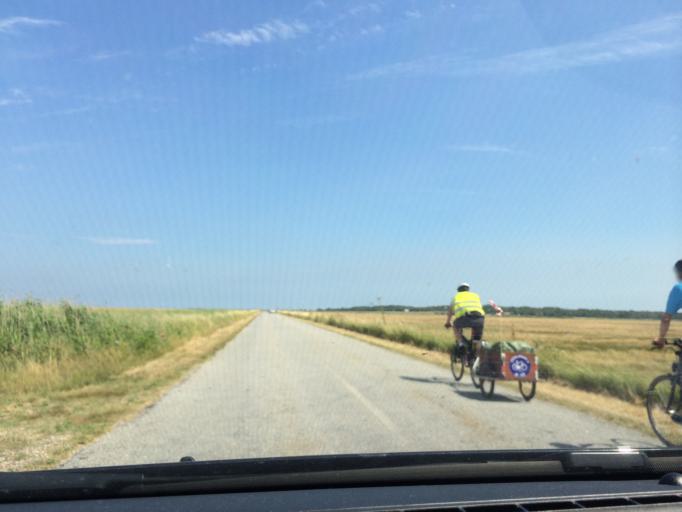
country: DK
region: Zealand
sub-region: Vordingborg Kommune
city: Stege
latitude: 55.0491
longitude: 12.2204
